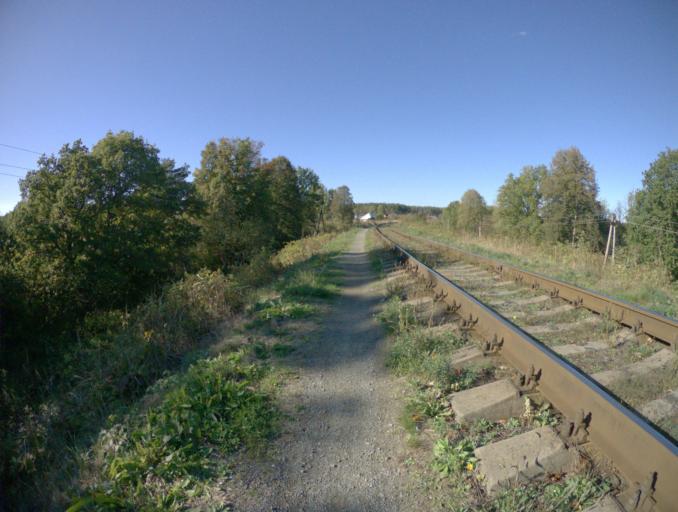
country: RU
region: Vladimir
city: Raduzhnyy
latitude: 56.0551
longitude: 40.3714
